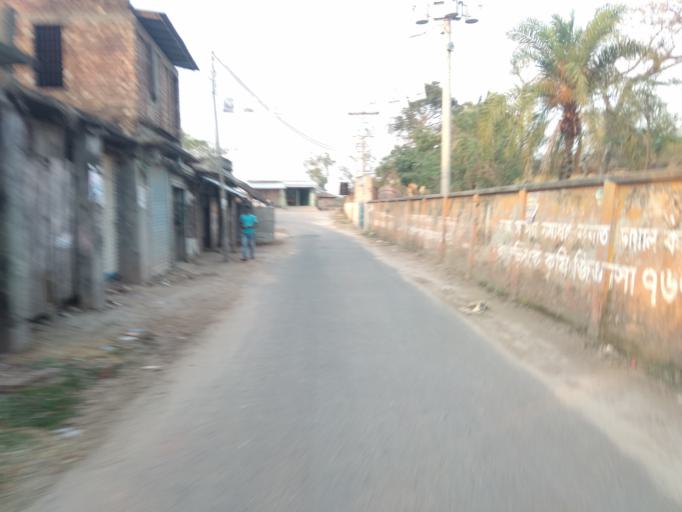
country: BD
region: Khulna
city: Satkhira
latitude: 22.5478
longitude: 89.1737
